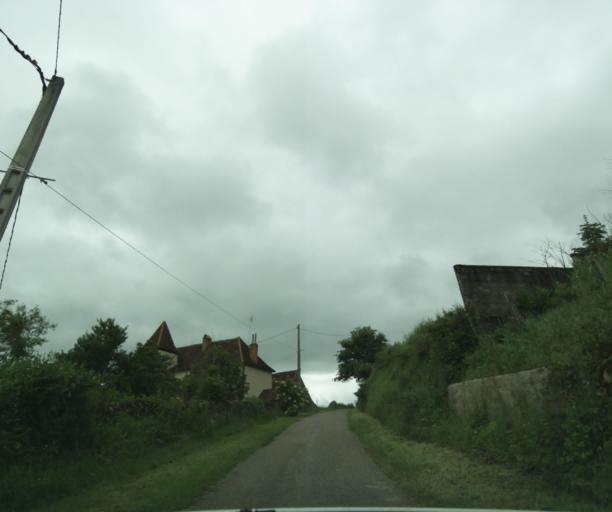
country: FR
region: Bourgogne
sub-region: Departement de Saone-et-Loire
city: Charolles
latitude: 46.4464
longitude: 4.2700
